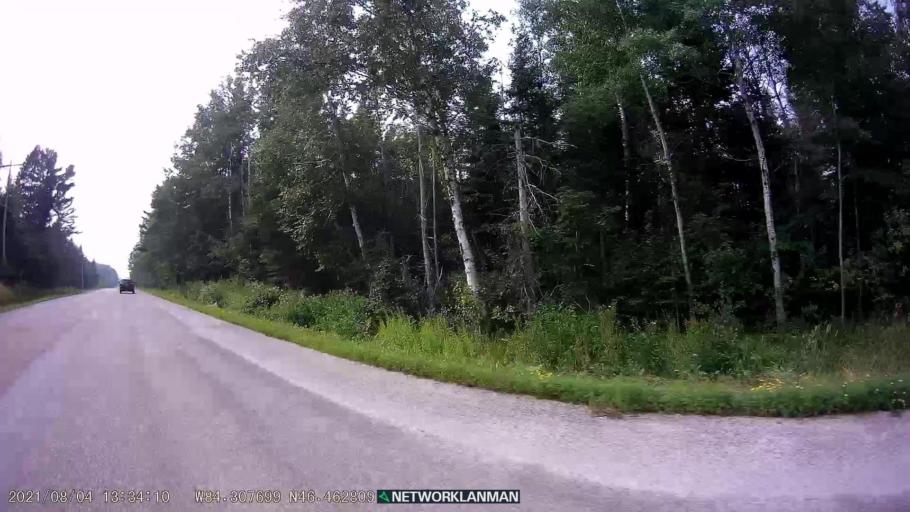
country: US
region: Michigan
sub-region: Chippewa County
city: Sault Ste. Marie
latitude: 46.4628
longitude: -84.3082
